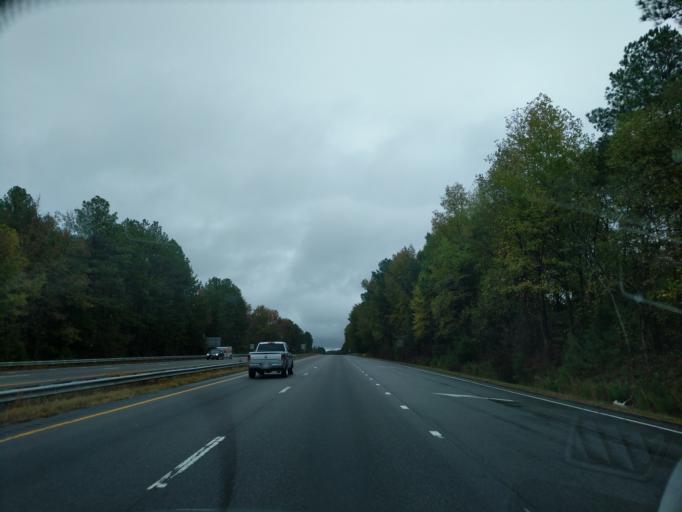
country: US
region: North Carolina
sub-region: Durham County
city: Gorman
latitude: 36.0330
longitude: -78.8393
